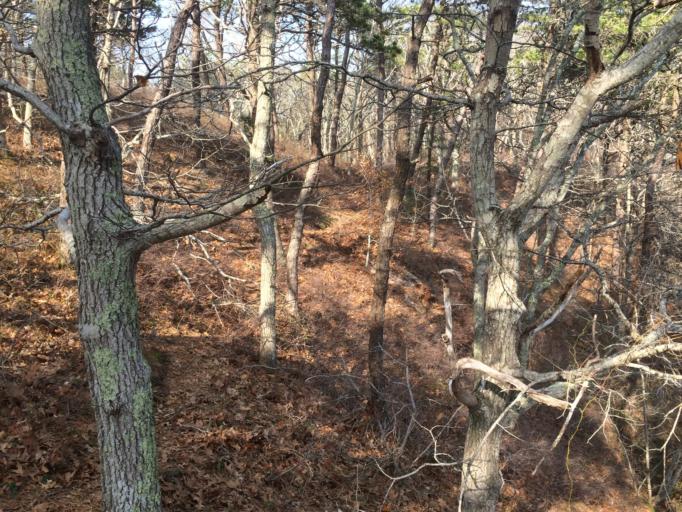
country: US
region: Massachusetts
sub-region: Barnstable County
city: Provincetown
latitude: 42.0568
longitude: -70.1968
